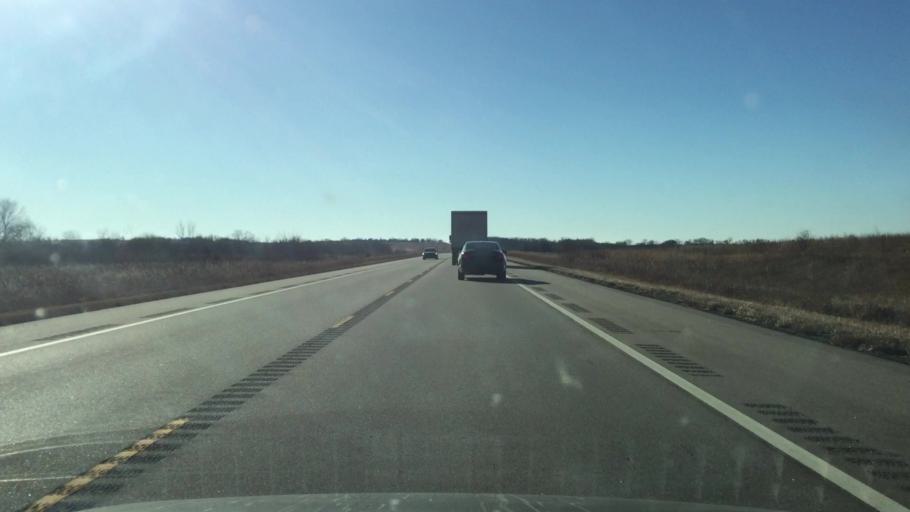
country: US
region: Kansas
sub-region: Allen County
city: Iola
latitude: 38.0296
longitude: -95.3806
